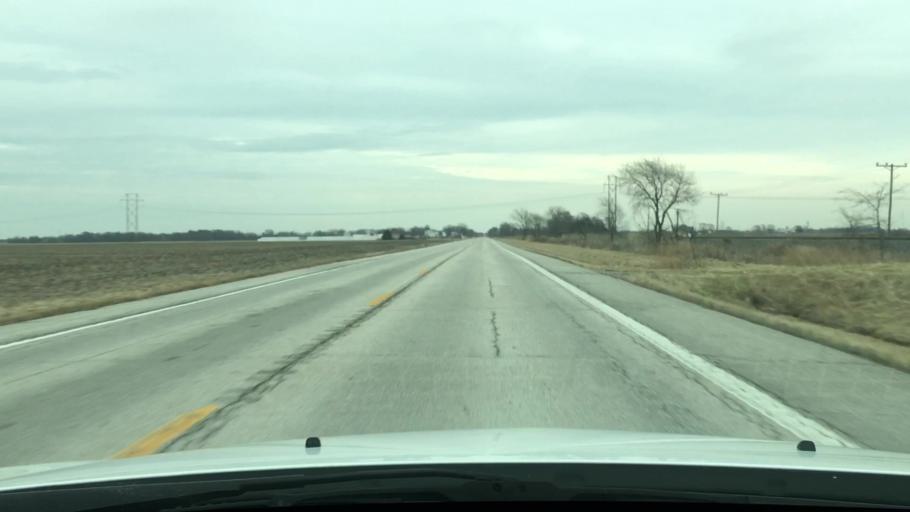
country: US
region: Missouri
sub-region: Audrain County
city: Vandalia
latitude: 39.2888
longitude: -91.5369
